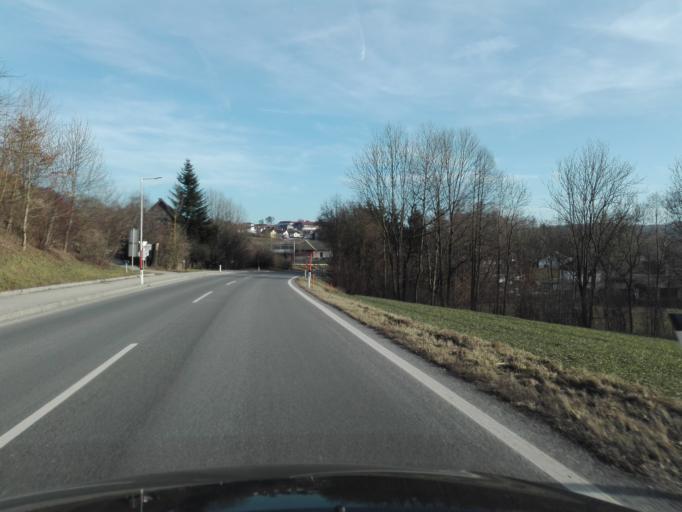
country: AT
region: Lower Austria
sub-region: Politischer Bezirk Amstetten
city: Amstetten
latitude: 48.1735
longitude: 14.8329
